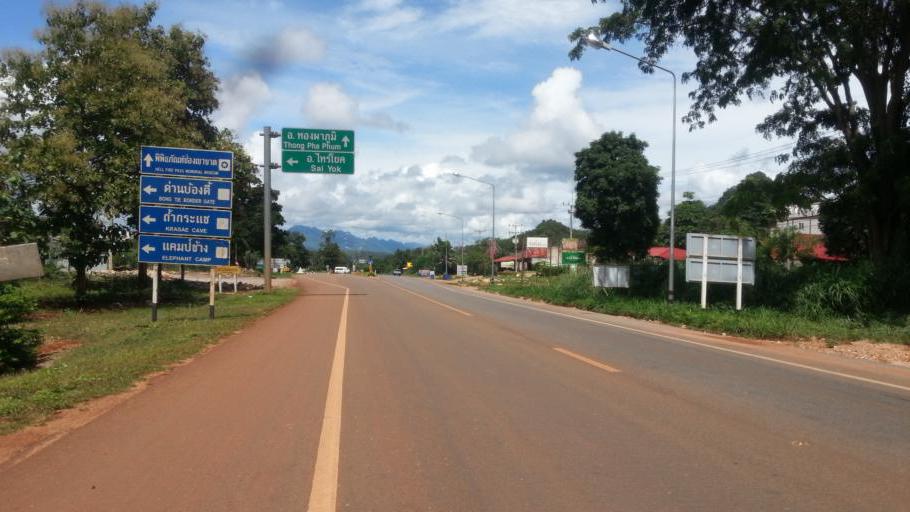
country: TH
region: Kanchanaburi
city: Sai Yok
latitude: 14.1290
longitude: 99.1656
